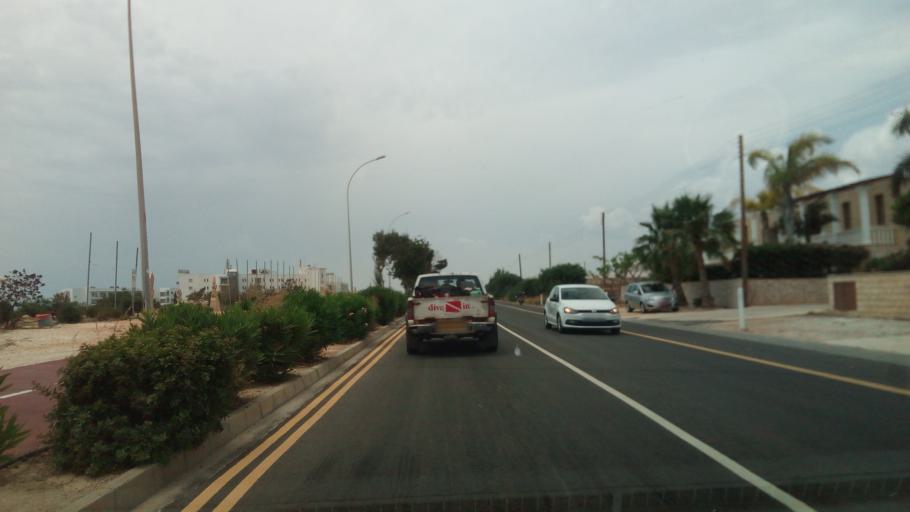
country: CY
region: Ammochostos
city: Ayia Napa
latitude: 34.9857
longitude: 34.0193
